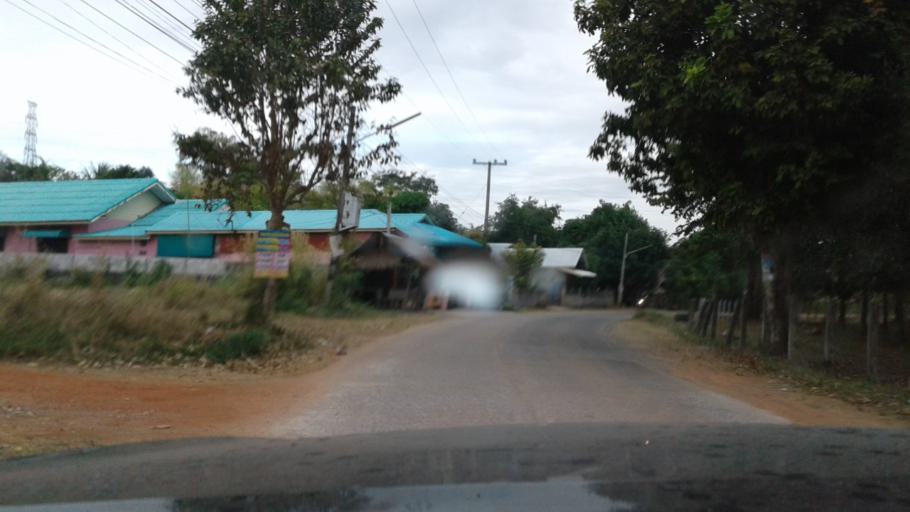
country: TH
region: Changwat Udon Thani
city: Nong Wua So
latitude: 17.2374
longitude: 102.5336
